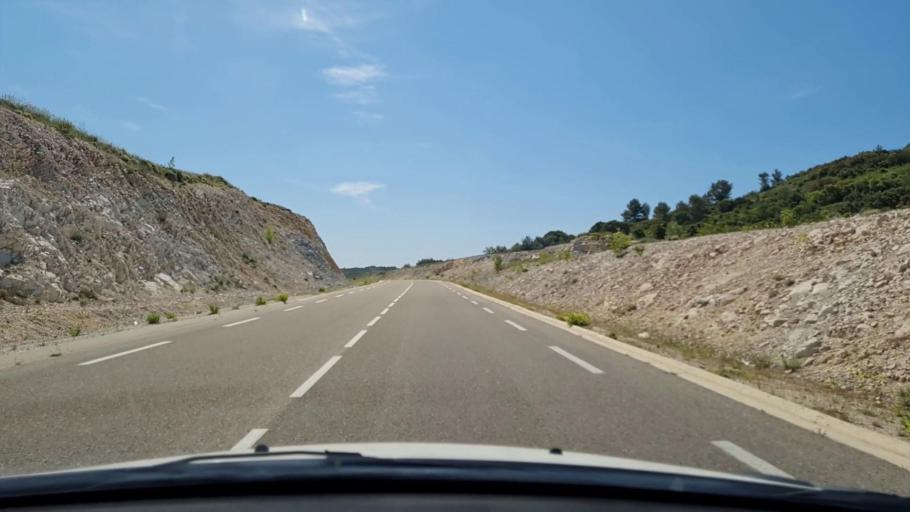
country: FR
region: Languedoc-Roussillon
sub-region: Departement du Gard
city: La Calmette
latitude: 43.9077
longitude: 4.2732
